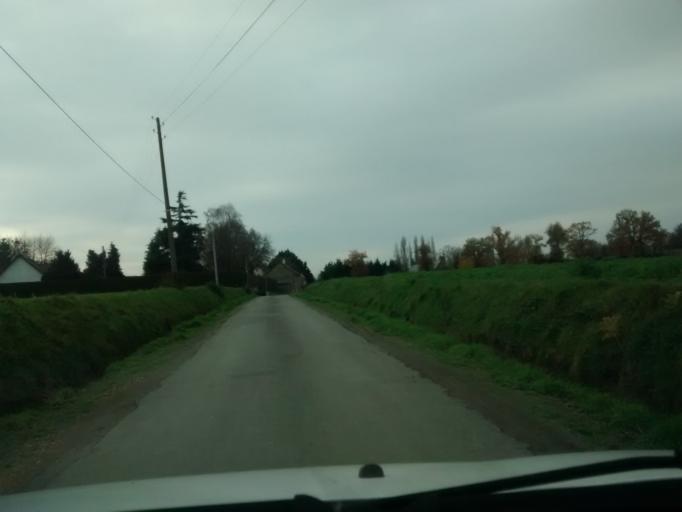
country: FR
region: Brittany
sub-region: Departement d'Ille-et-Vilaine
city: Acigne
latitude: 48.1119
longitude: -1.5504
